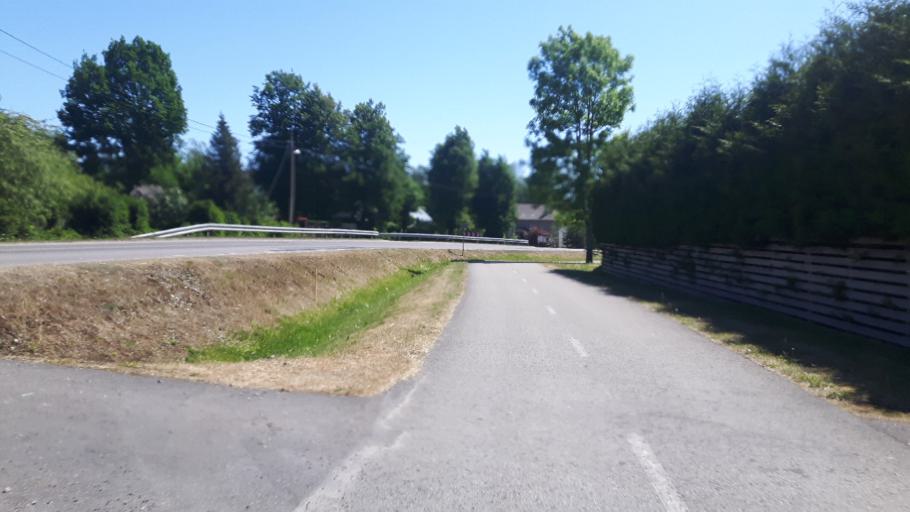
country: EE
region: Harju
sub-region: Saku vald
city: Saku
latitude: 59.2415
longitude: 24.6805
